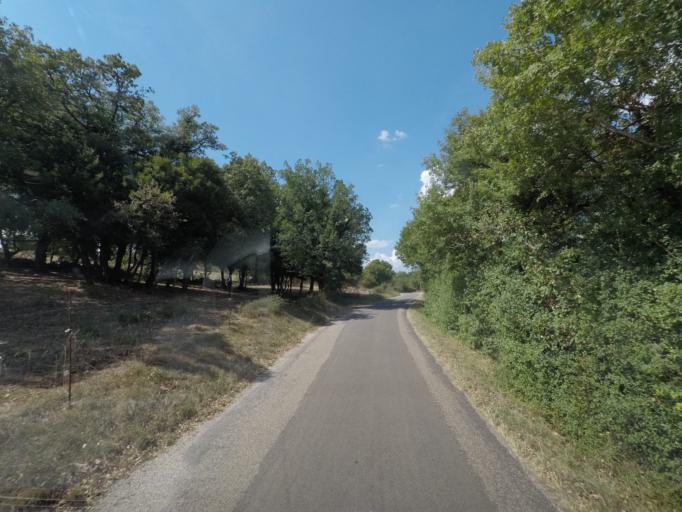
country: FR
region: Midi-Pyrenees
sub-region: Departement du Lot
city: Lalbenque
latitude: 44.5197
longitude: 1.6274
